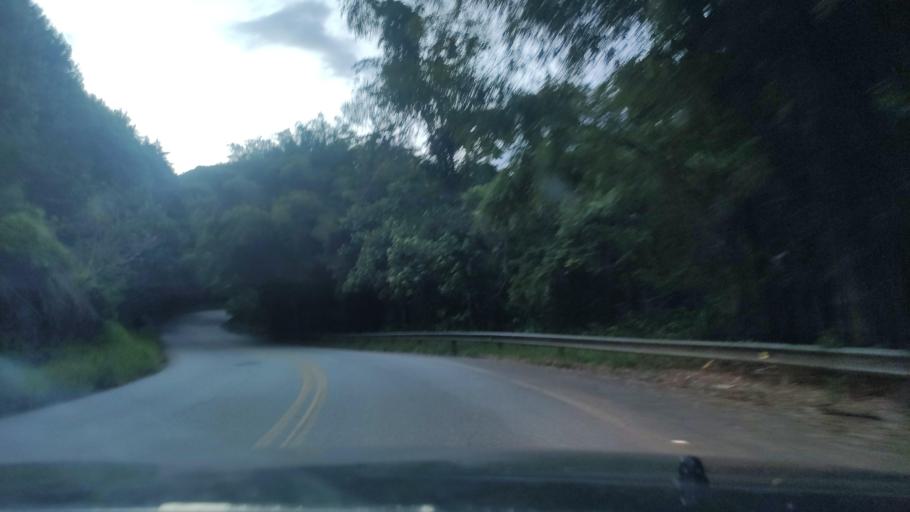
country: BR
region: Sao Paulo
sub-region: Campos Do Jordao
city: Campos do Jordao
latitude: -22.8211
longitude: -45.7459
